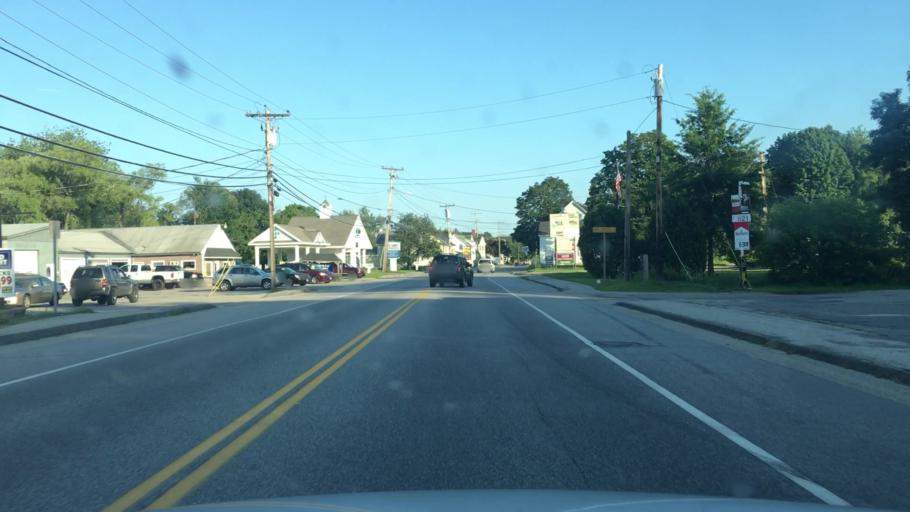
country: US
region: Maine
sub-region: Androscoggin County
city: Lisbon
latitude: 44.0340
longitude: -70.1063
